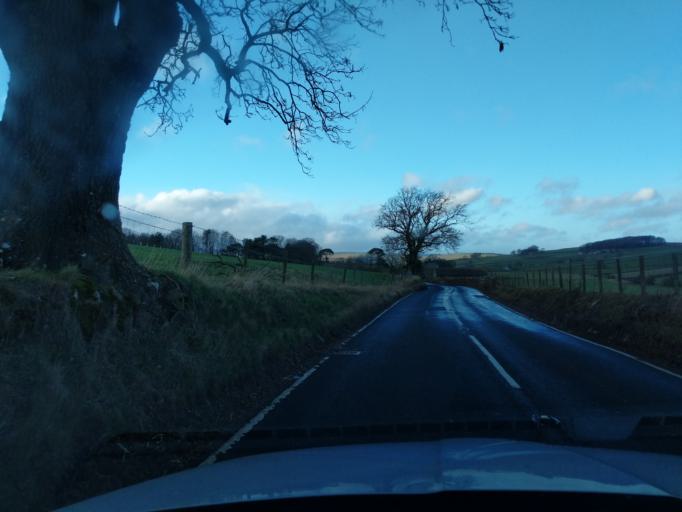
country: GB
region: England
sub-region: North Yorkshire
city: Leyburn
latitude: 54.3528
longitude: -1.8116
